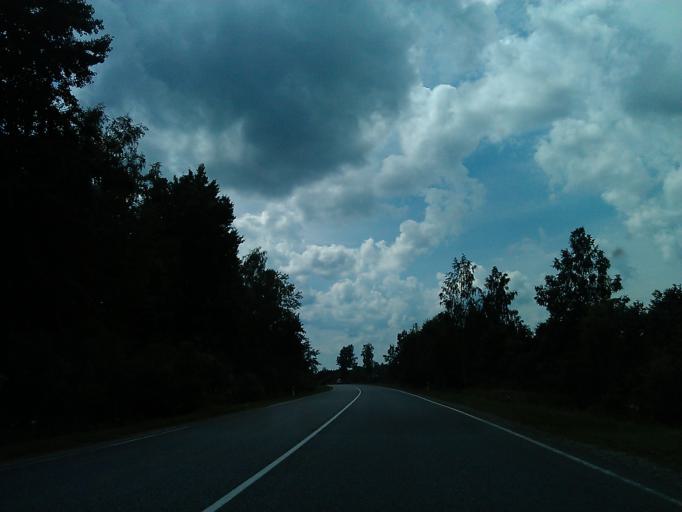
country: LV
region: Jaunpils
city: Jaunpils
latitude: 56.6641
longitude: 22.9835
